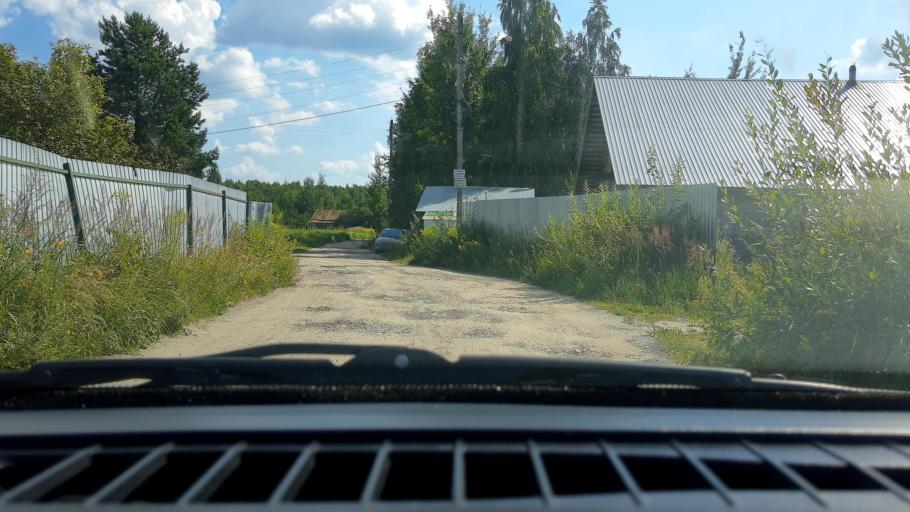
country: RU
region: Nizjnij Novgorod
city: Gorbatovka
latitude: 56.3346
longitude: 43.6667
